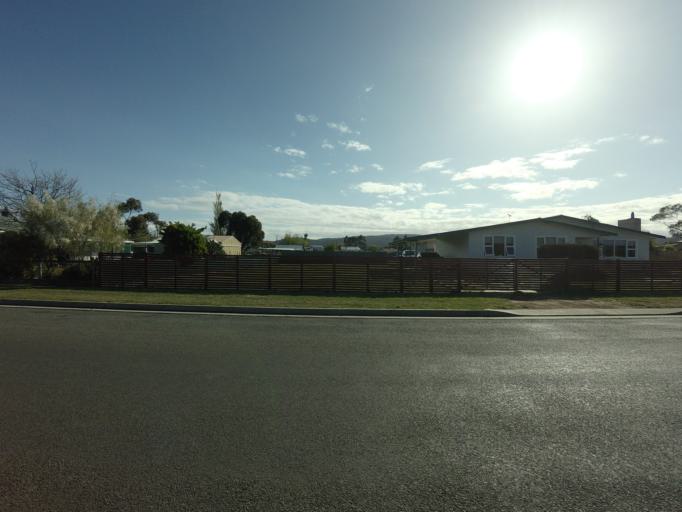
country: AU
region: Tasmania
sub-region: Sorell
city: Sorell
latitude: -42.5070
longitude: 147.9162
